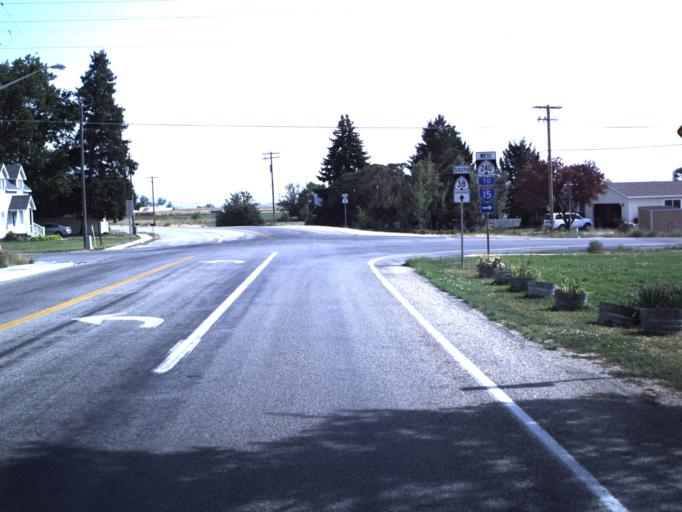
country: US
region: Utah
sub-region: Box Elder County
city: Honeyville
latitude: 41.6352
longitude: -112.0796
